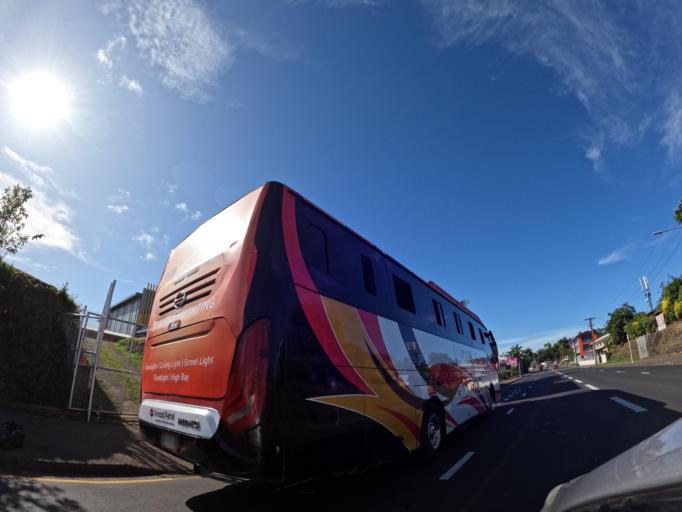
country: FJ
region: Central
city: Suva
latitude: -18.1449
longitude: 178.4476
